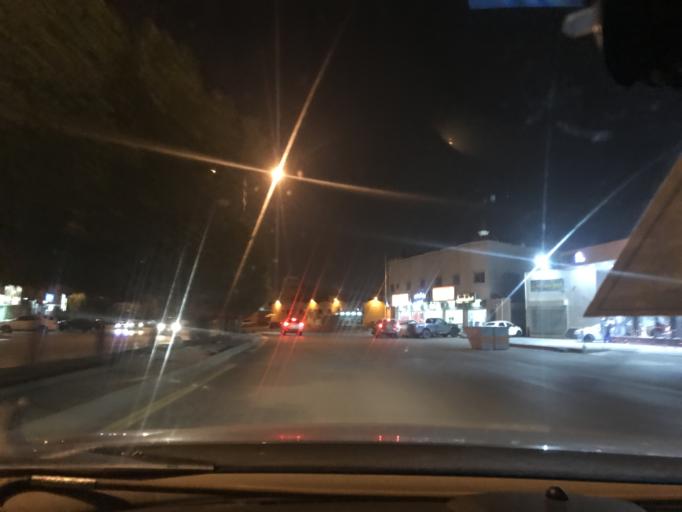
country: SA
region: Ar Riyad
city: Riyadh
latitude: 24.7462
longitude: 46.7532
